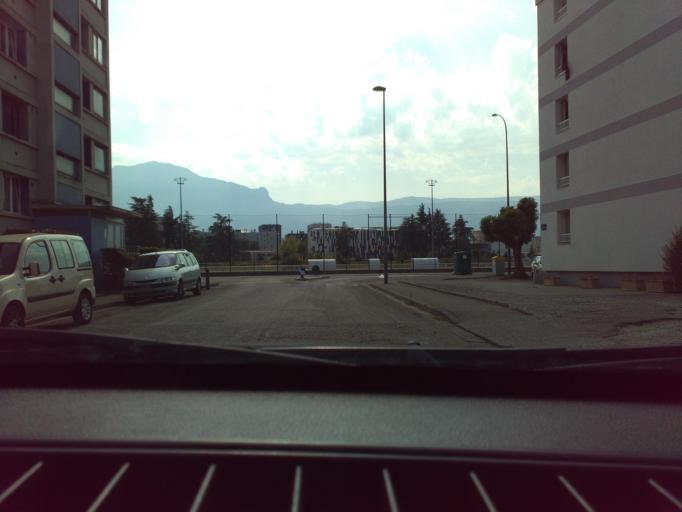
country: FR
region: Rhone-Alpes
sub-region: Departement de l'Isere
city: Saint-Martin-d'Heres
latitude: 45.1770
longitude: 5.7483
